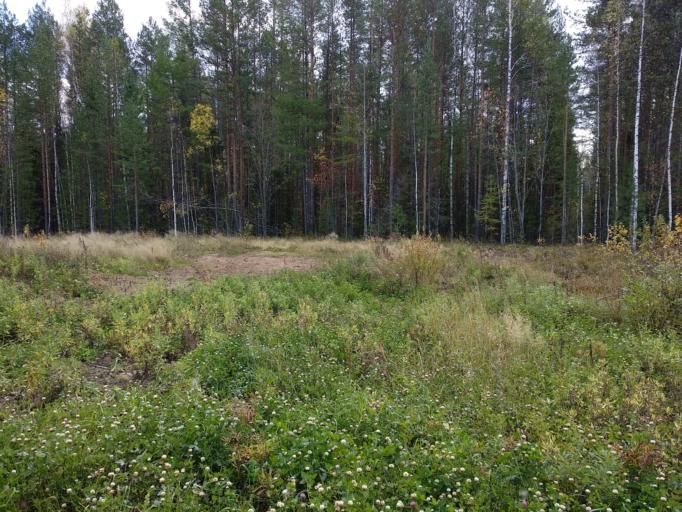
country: RU
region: Sverdlovsk
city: Rudnichnyy
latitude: 59.9348
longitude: 60.4573
